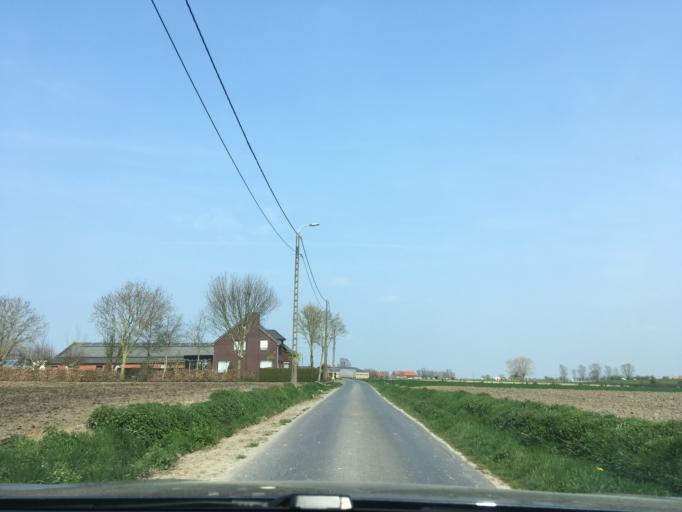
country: BE
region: Flanders
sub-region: Provincie West-Vlaanderen
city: Ardooie
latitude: 51.0058
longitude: 3.1841
